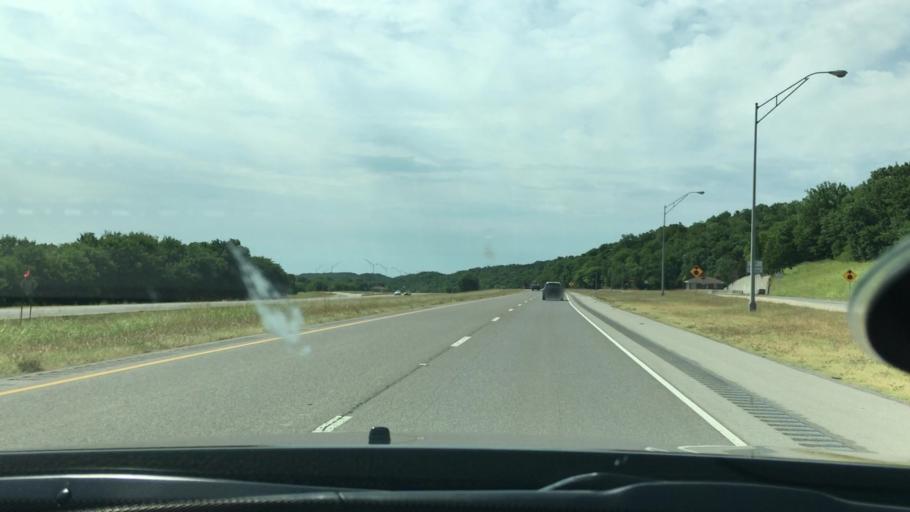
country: US
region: Oklahoma
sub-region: Murray County
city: Davis
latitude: 34.4795
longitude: -97.1577
